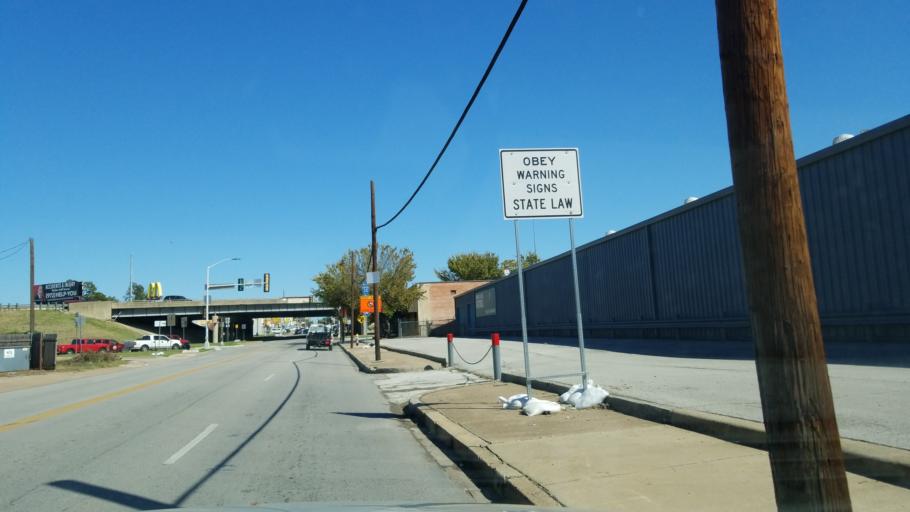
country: US
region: Texas
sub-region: Dallas County
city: Dallas
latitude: 32.7902
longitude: -96.7513
